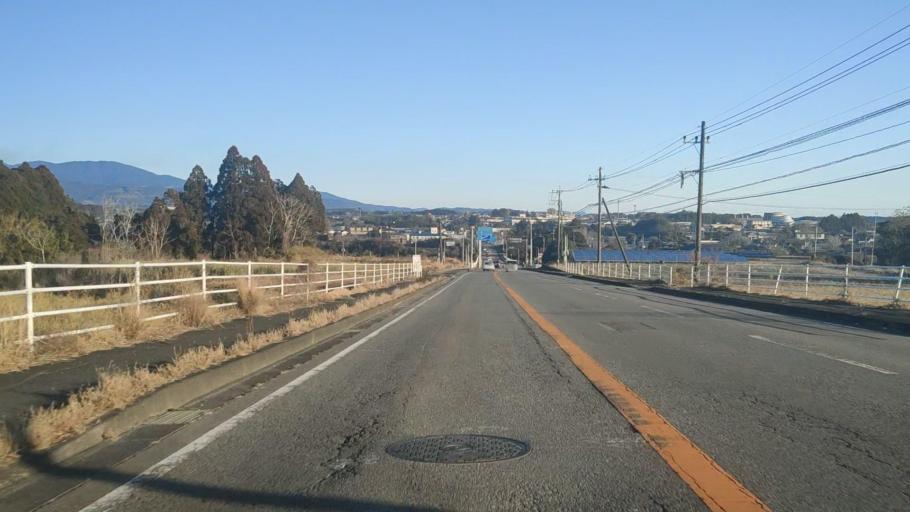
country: JP
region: Miyazaki
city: Takanabe
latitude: 32.1817
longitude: 131.5220
